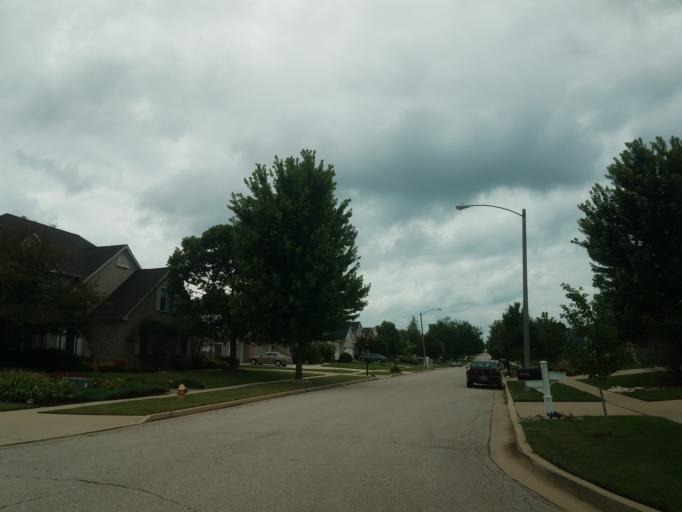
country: US
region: Illinois
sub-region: McLean County
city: Twin Grove
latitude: 40.4506
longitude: -89.0481
